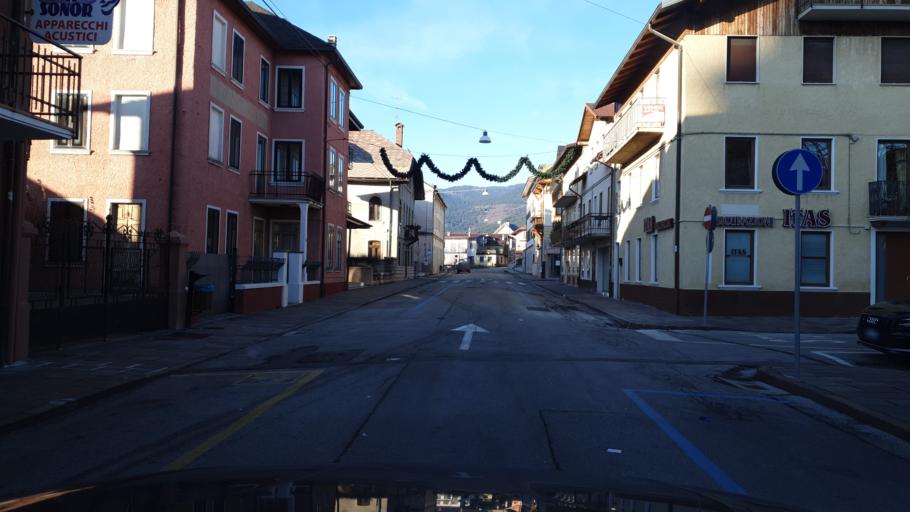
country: IT
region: Veneto
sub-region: Provincia di Vicenza
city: Asiago
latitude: 45.8769
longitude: 11.5088
